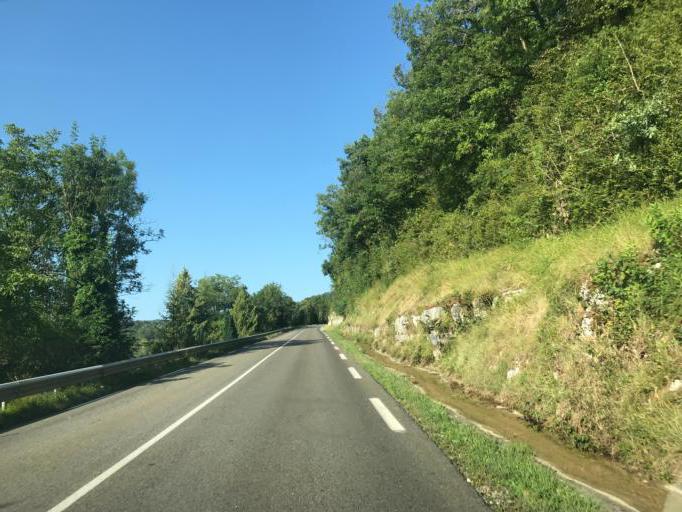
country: FR
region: Franche-Comte
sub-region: Departement du Jura
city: Lavans-les-Saint-Claude
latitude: 46.3858
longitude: 5.7776
